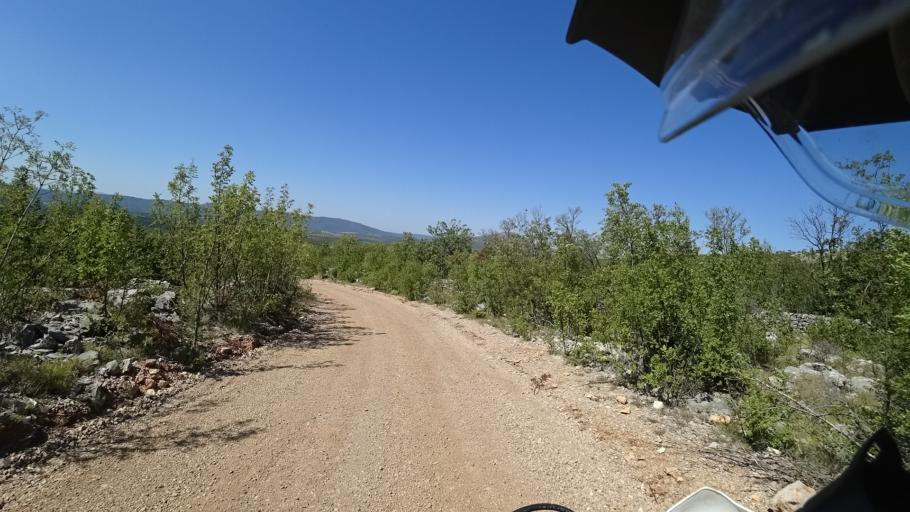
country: HR
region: Splitsko-Dalmatinska
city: Hrvace
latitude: 43.7546
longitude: 16.4524
